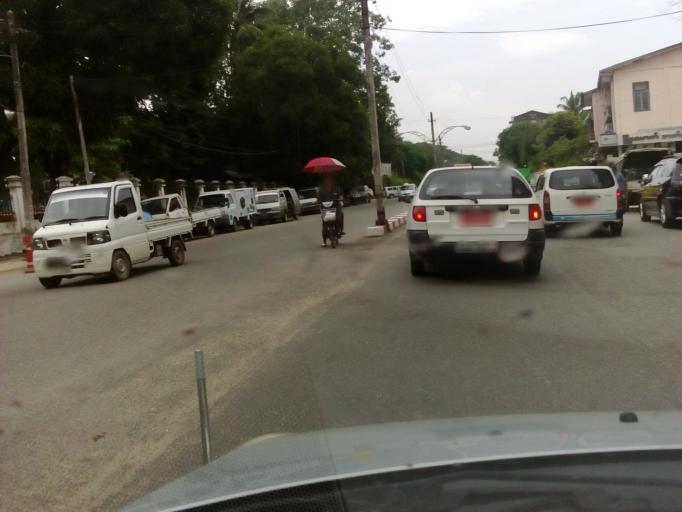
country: MM
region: Yangon
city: Yangon
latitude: 16.8036
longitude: 96.1743
